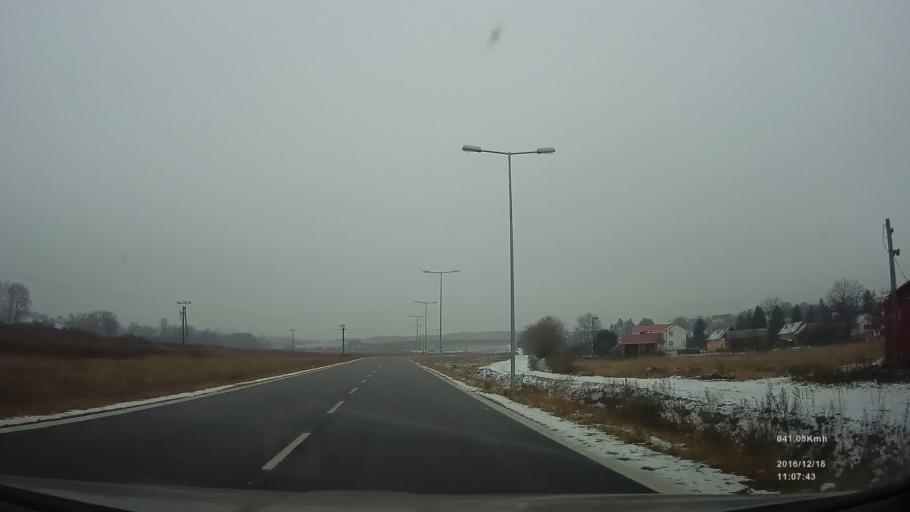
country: SK
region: Kosicky
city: Kosice
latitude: 48.8314
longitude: 21.3124
